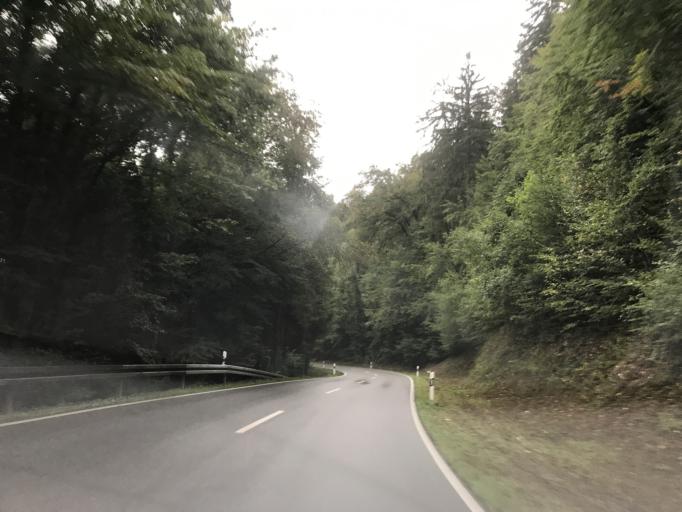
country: DE
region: Baden-Wuerttemberg
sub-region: Freiburg Region
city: Schworstadt
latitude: 47.5957
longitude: 7.8666
